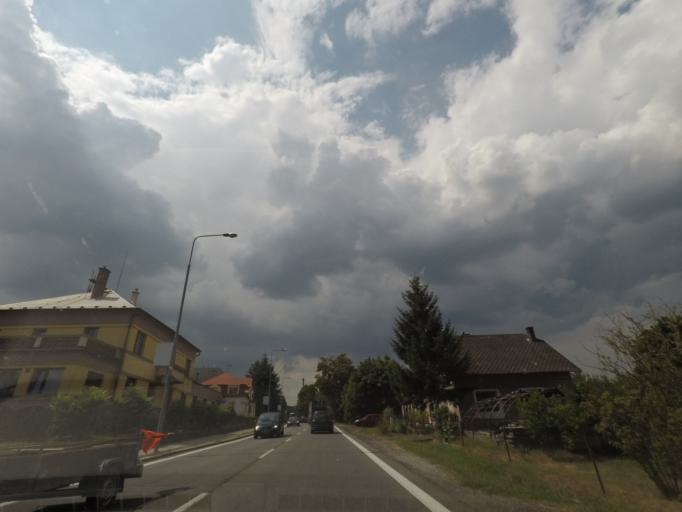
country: CZ
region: Kralovehradecky
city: Nova Paka
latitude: 50.4882
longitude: 15.5158
